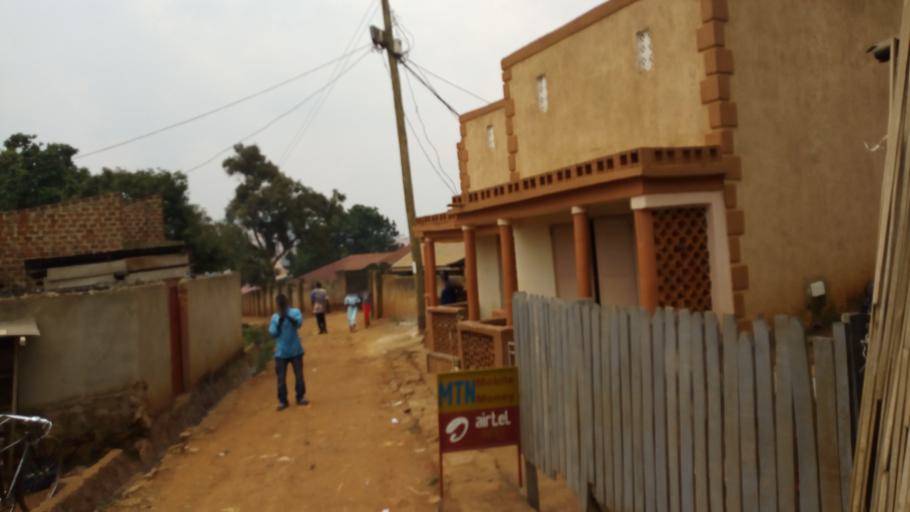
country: UG
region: Central Region
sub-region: Wakiso District
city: Kireka
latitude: 0.3249
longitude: 32.6424
